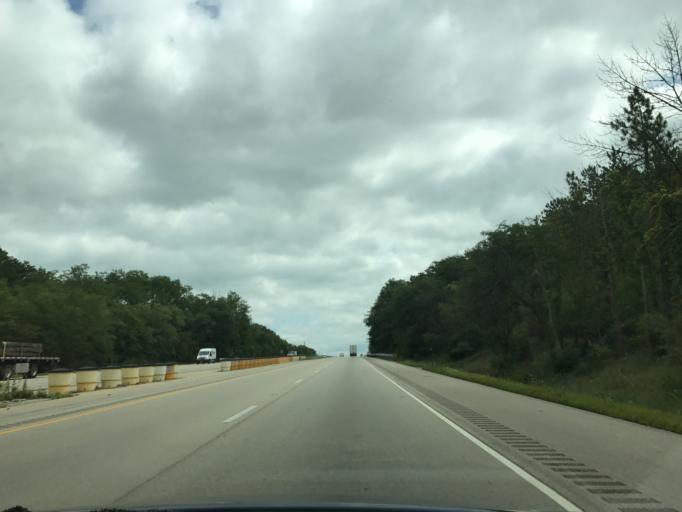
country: US
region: Illinois
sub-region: LaSalle County
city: Ottawa
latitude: 41.3772
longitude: -88.7894
